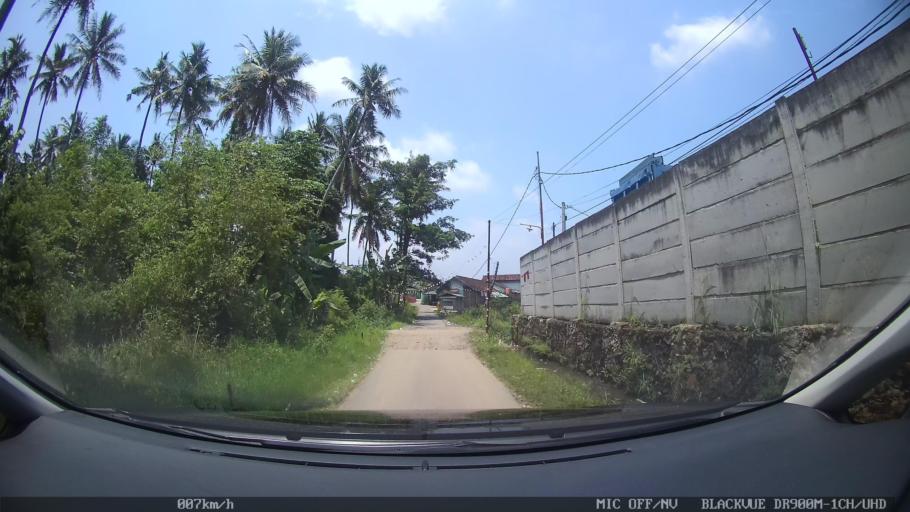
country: ID
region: Lampung
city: Kedaton
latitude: -5.3650
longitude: 105.2636
